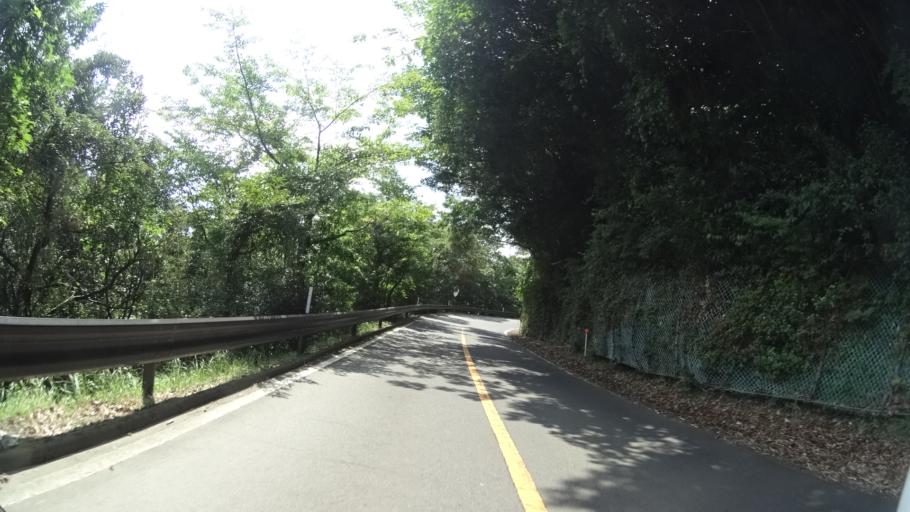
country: JP
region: Miyazaki
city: Kobayashi
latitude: 31.9015
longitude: 130.8405
